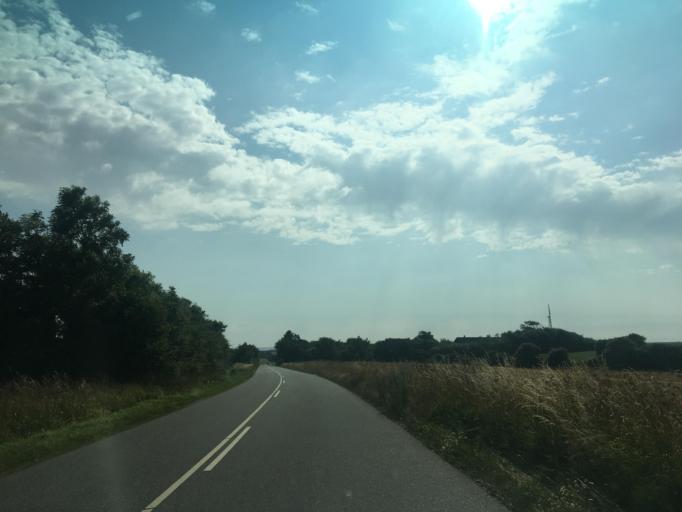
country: DK
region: North Denmark
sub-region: Thisted Kommune
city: Hurup
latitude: 56.8338
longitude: 8.5686
